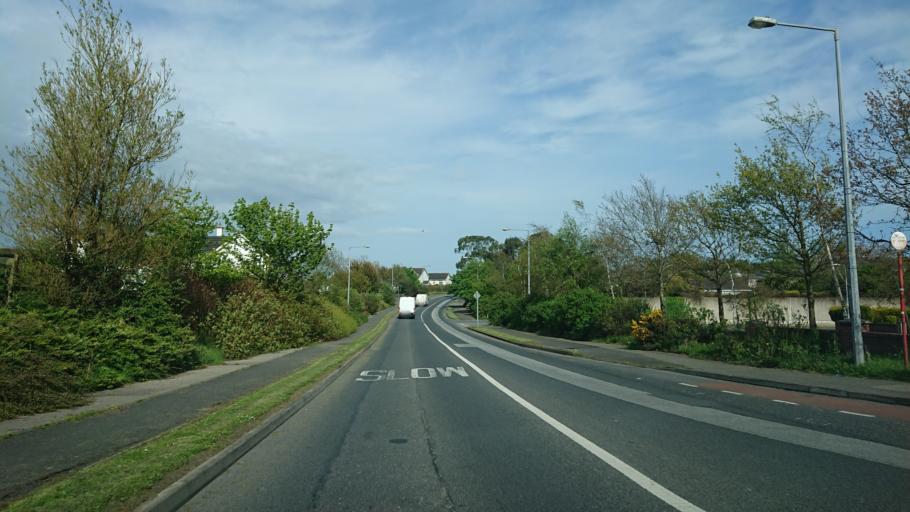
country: IE
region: Munster
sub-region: Waterford
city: Waterford
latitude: 52.2645
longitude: -7.1407
